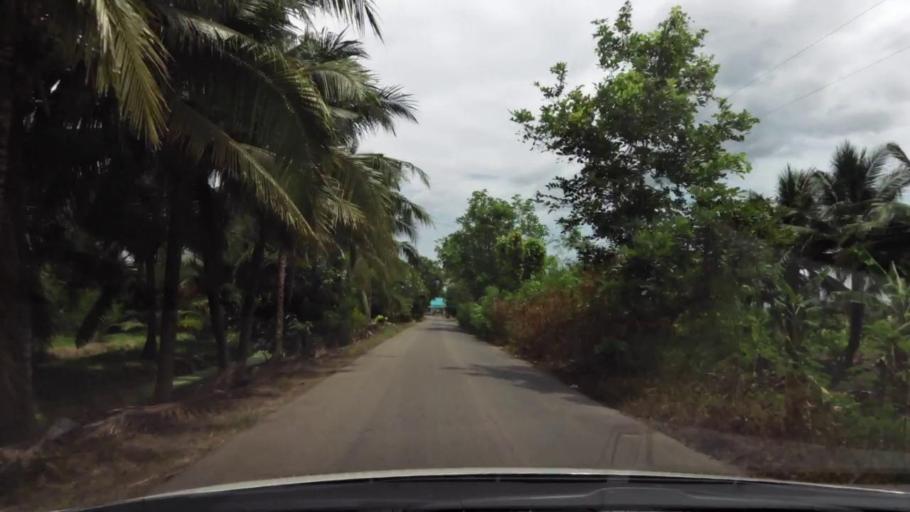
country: TH
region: Ratchaburi
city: Damnoen Saduak
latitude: 13.5368
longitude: 99.9988
